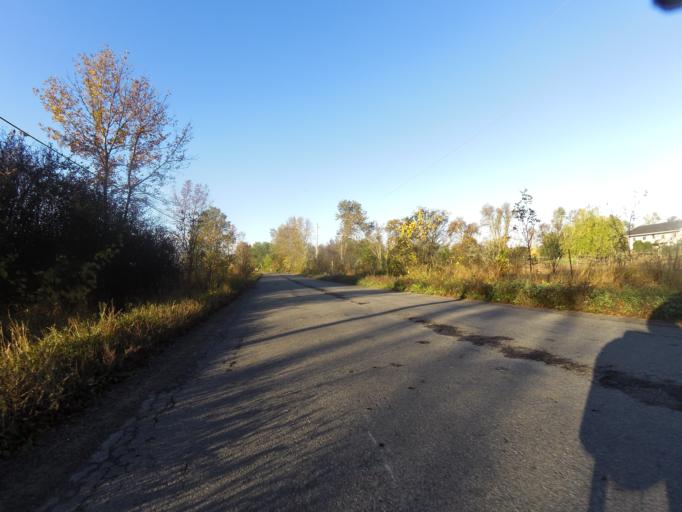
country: CA
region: Ontario
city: Quinte West
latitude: 44.0232
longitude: -77.4907
